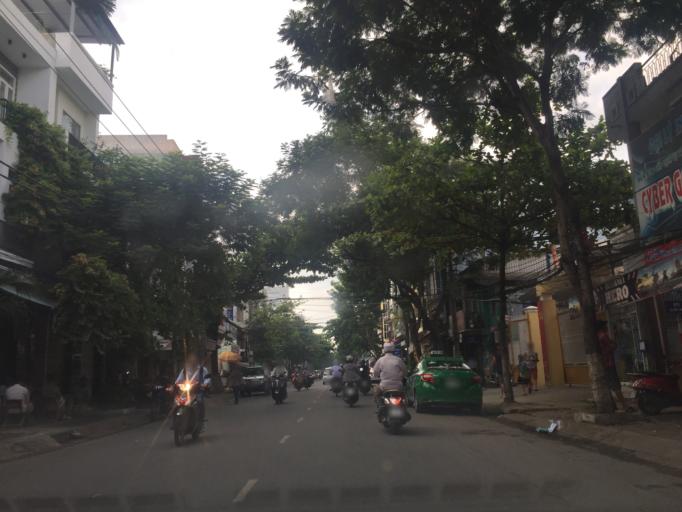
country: VN
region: Da Nang
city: Da Nang
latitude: 16.0771
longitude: 108.2121
